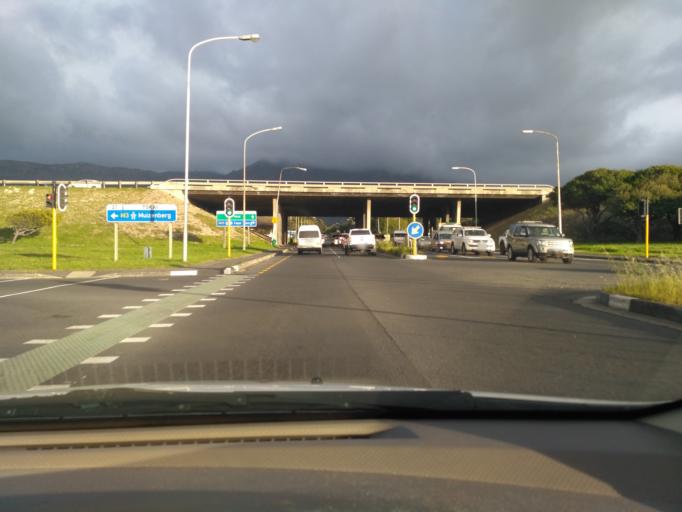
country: ZA
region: Western Cape
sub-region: City of Cape Town
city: Bergvliet
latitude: -34.0647
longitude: 18.4498
